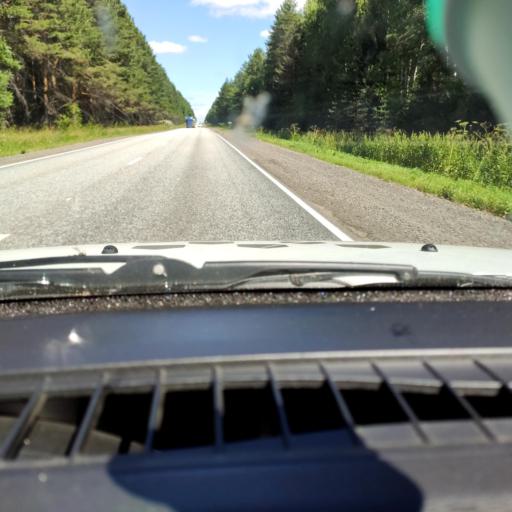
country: RU
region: Udmurtiya
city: Khokhryaki
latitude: 56.9458
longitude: 53.6072
